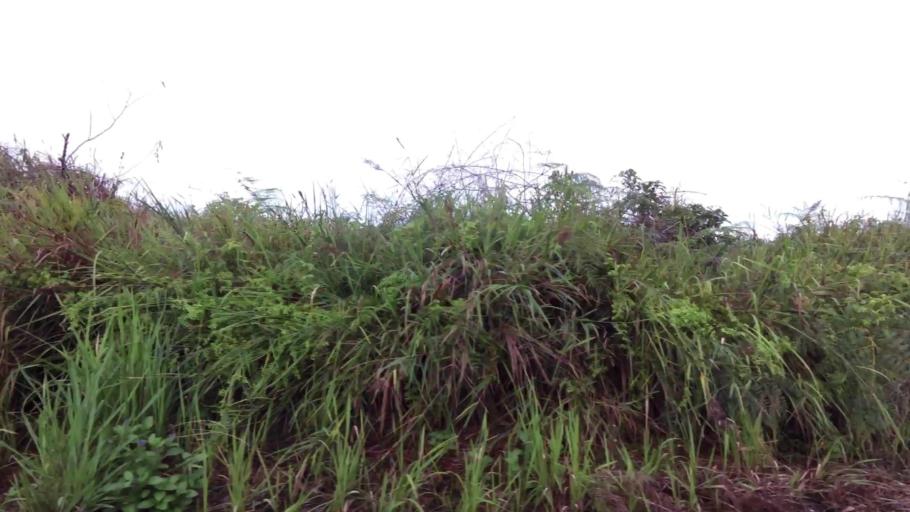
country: BN
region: Belait
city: Seria
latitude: 4.6050
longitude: 114.3304
